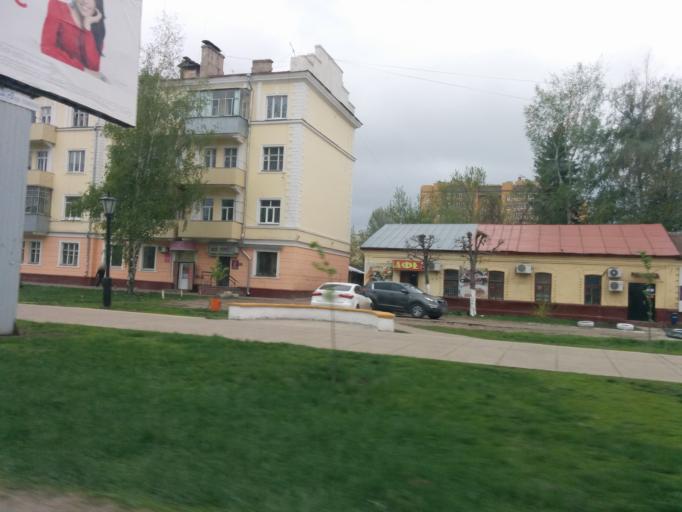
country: RU
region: Tambov
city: Tambov
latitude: 52.7207
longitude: 41.4375
